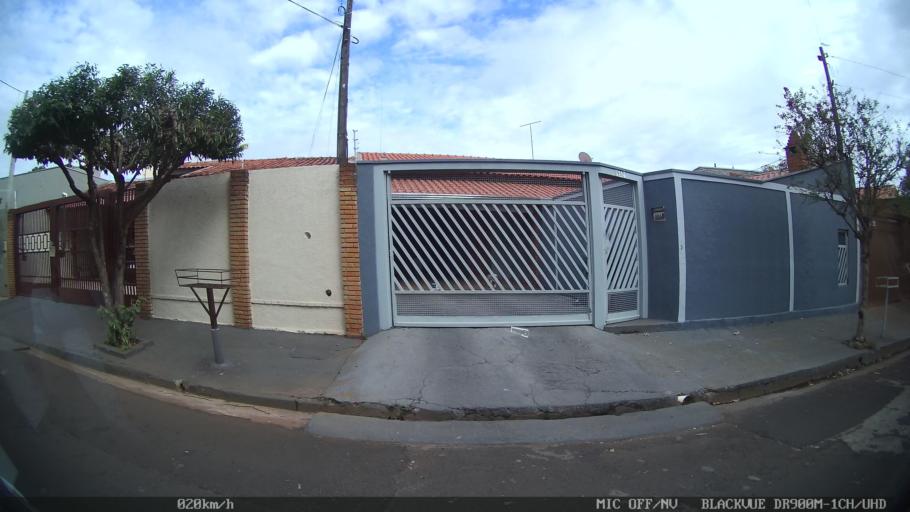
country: BR
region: Sao Paulo
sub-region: Sao Jose Do Rio Preto
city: Sao Jose do Rio Preto
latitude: -20.8206
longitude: -49.3490
